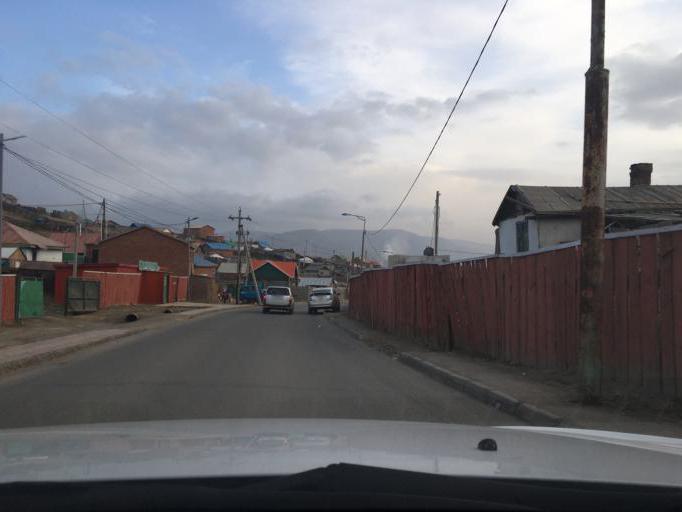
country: MN
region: Ulaanbaatar
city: Ulaanbaatar
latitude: 47.9298
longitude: 106.8584
